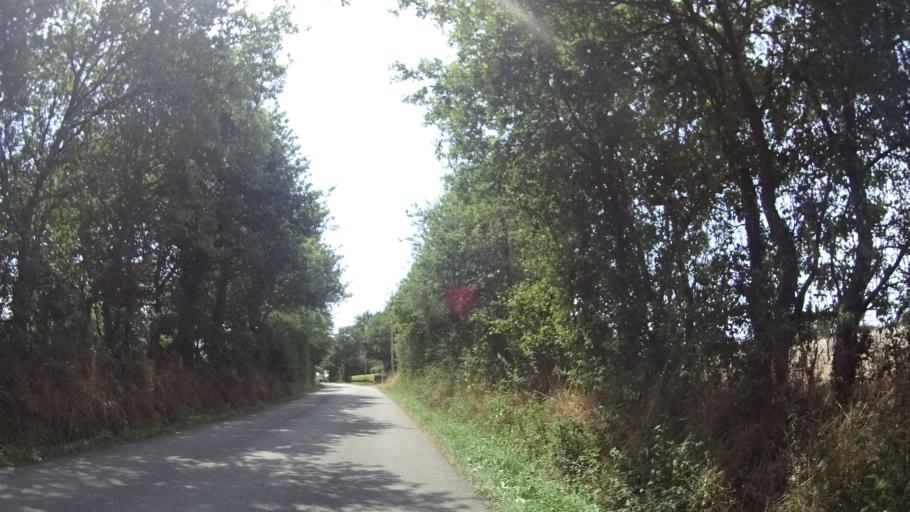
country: FR
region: Pays de la Loire
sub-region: Departement de la Loire-Atlantique
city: Bouvron
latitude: 47.3992
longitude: -1.8203
